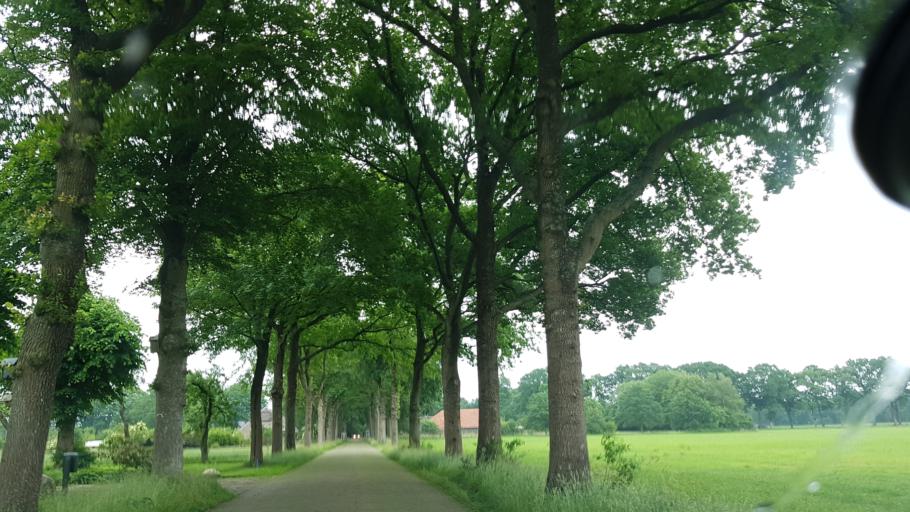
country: NL
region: Drenthe
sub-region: Gemeente Tynaarlo
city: Tynaarlo
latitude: 53.0493
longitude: 6.6346
